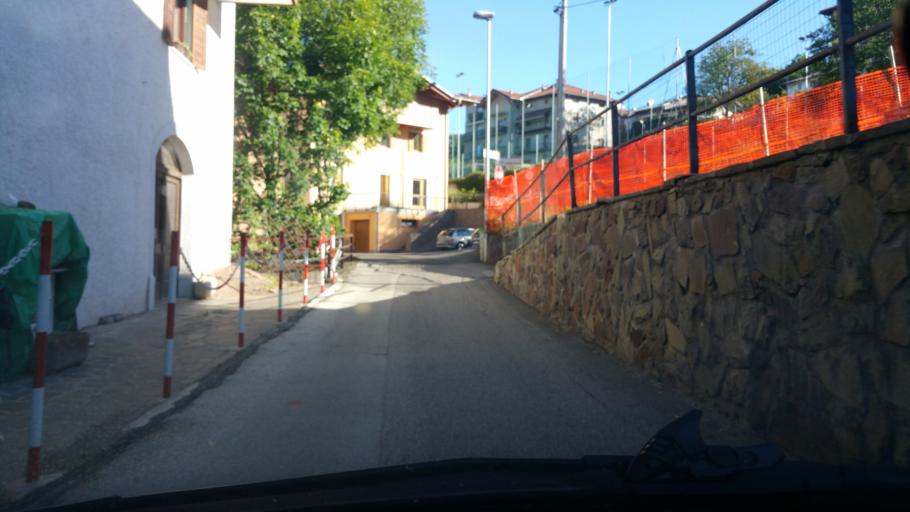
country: IT
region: Trentino-Alto Adige
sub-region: Provincia di Trento
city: Civezzano
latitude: 46.1059
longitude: 11.1846
